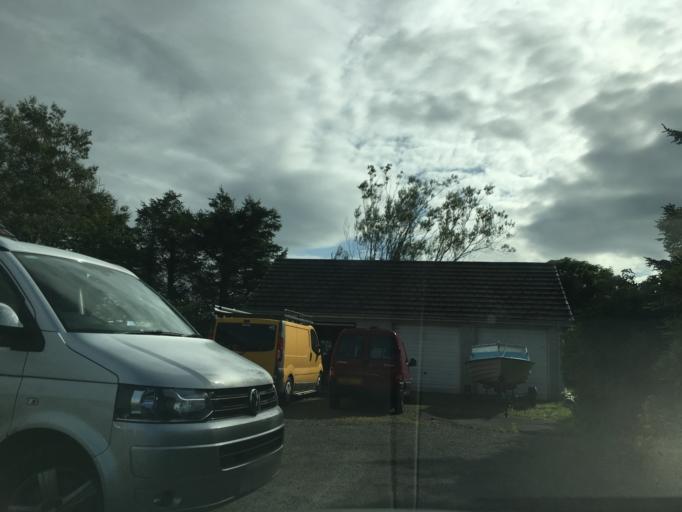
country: GB
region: Scotland
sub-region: Argyll and Bute
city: Oban
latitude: 56.2922
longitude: -5.6137
